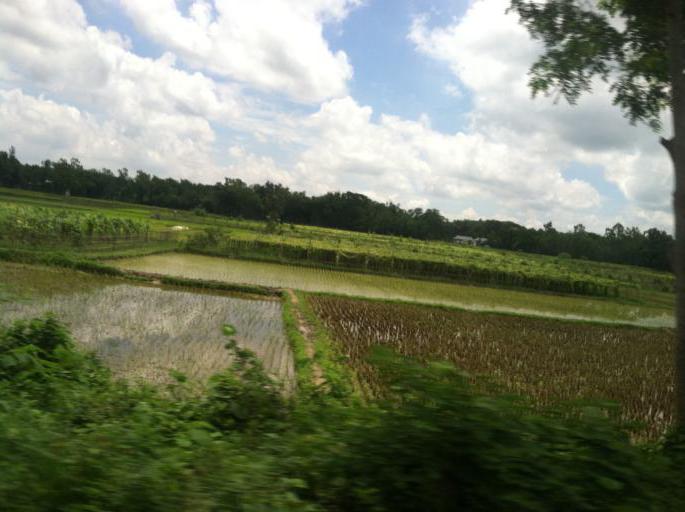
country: BD
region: Sylhet
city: Habiganj
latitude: 24.2048
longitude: 91.3522
